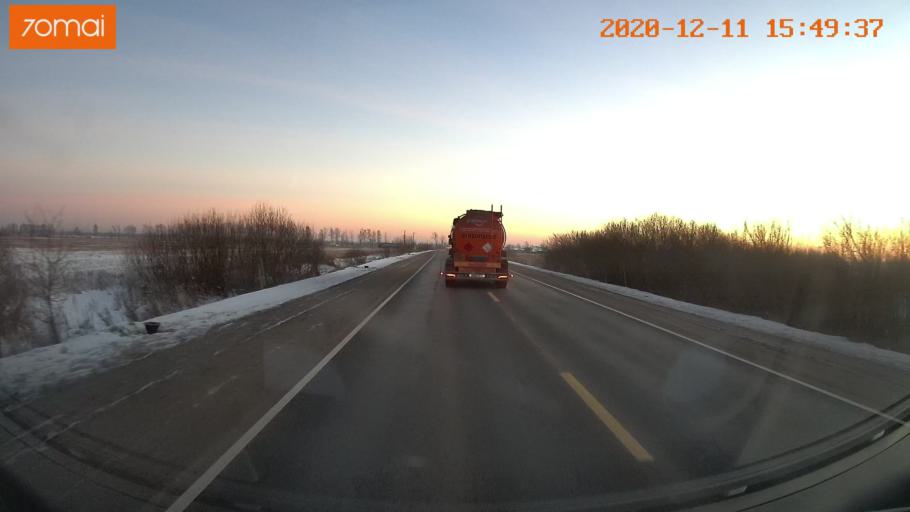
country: RU
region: Ivanovo
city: Novo-Talitsy
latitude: 56.9866
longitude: 40.8758
